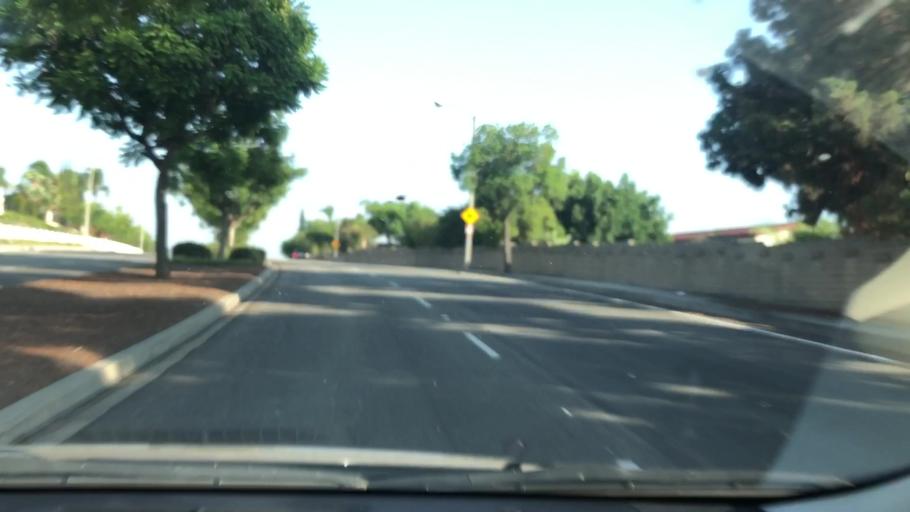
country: US
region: California
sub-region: Orange County
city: Yorba Linda
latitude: 33.8736
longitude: -117.7833
